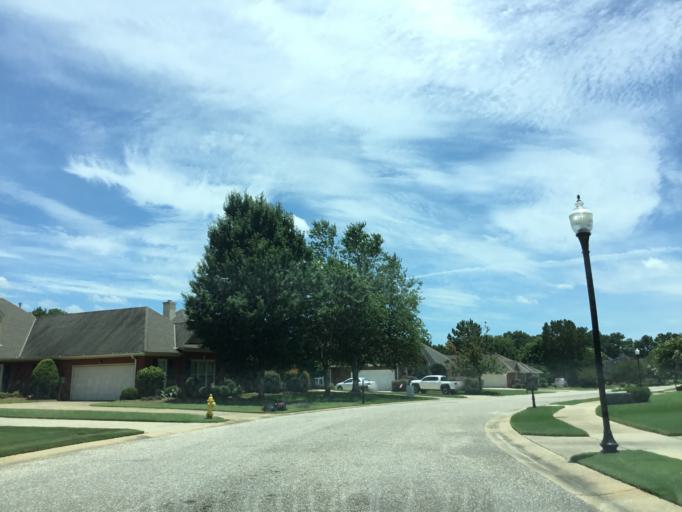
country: US
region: Alabama
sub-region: Montgomery County
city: Pike Road
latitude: 32.3765
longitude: -86.1408
